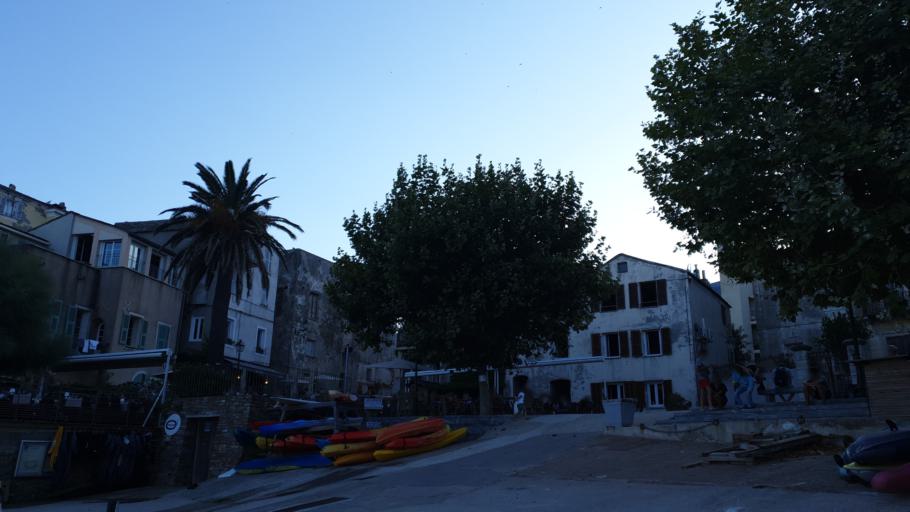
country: FR
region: Corsica
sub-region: Departement de la Haute-Corse
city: Brando
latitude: 42.7745
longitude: 9.4764
